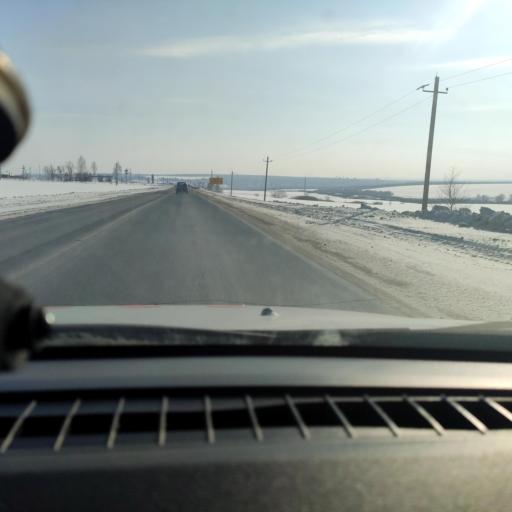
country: RU
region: Samara
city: Petra-Dubrava
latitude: 53.3094
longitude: 50.4574
